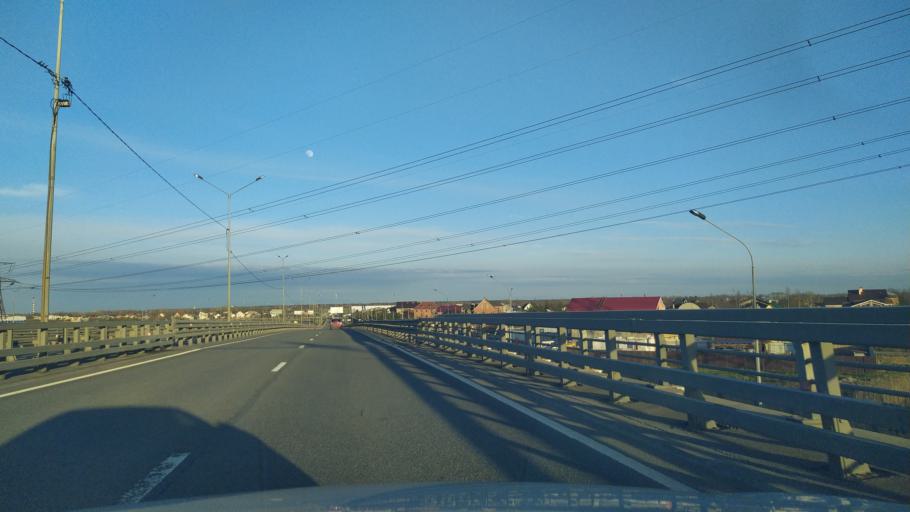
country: RU
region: St.-Petersburg
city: Aleksandrovskaya
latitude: 59.7439
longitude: 30.3117
